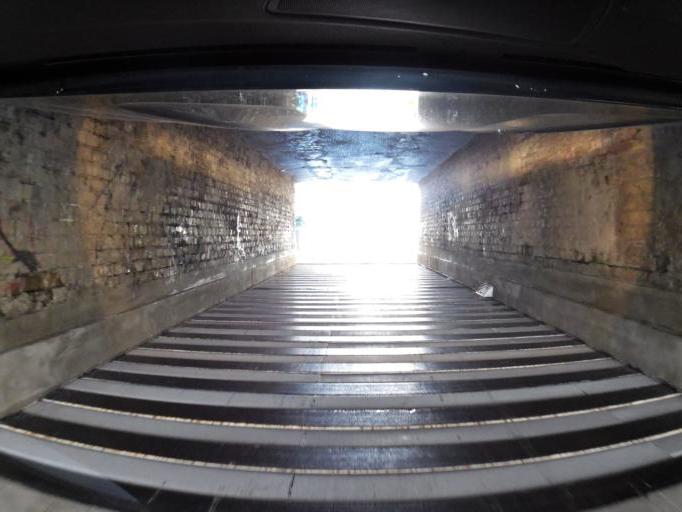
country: IT
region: The Marches
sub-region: Province of Fermo
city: Porto San Giorgio
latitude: 43.1829
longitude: 13.7959
